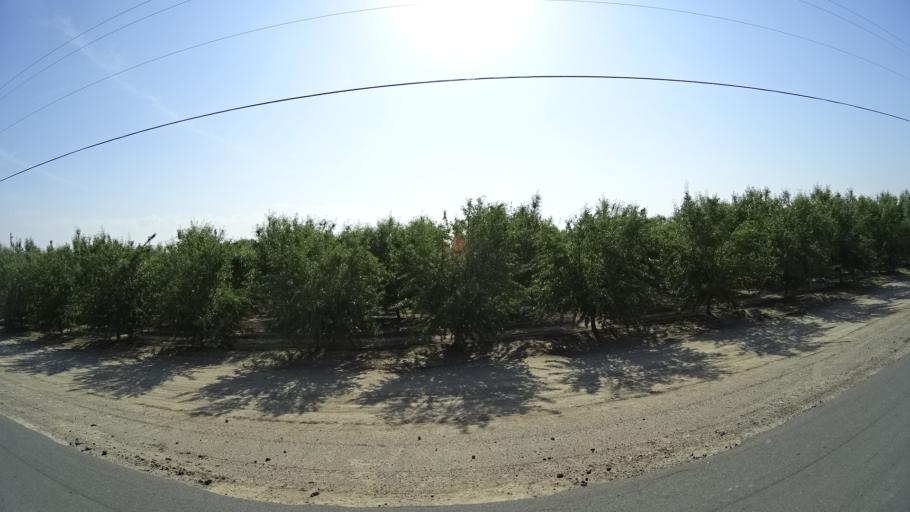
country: US
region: California
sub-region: Kings County
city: Lemoore
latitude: 36.3315
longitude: -119.8347
